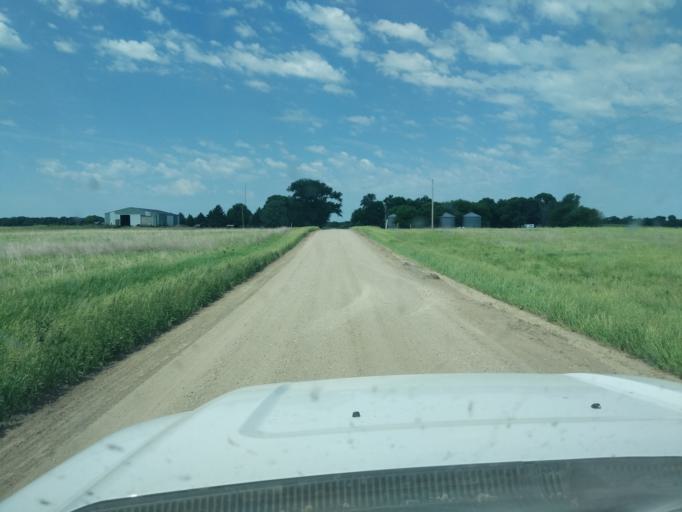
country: US
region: Minnesota
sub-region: Yellow Medicine County
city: Granite Falls
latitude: 44.7453
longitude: -95.3948
